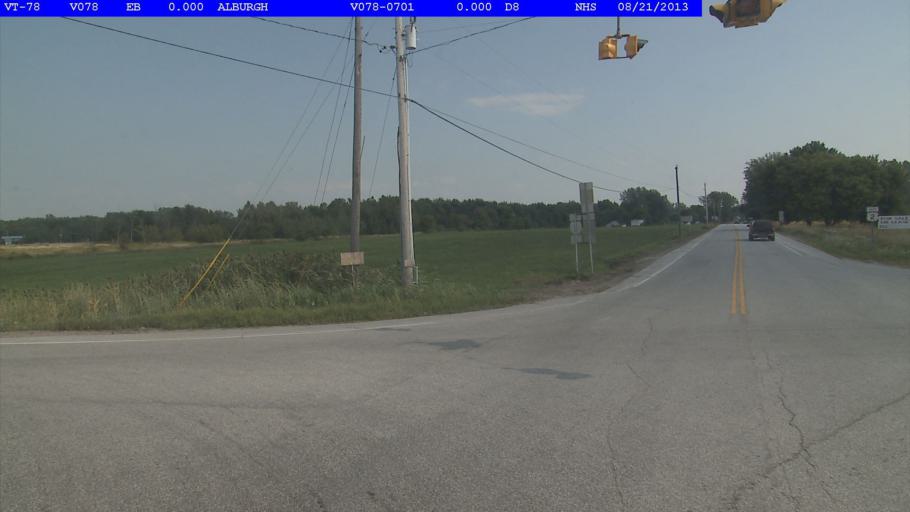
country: US
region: New York
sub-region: Clinton County
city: Rouses Point
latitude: 44.9598
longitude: -73.2771
